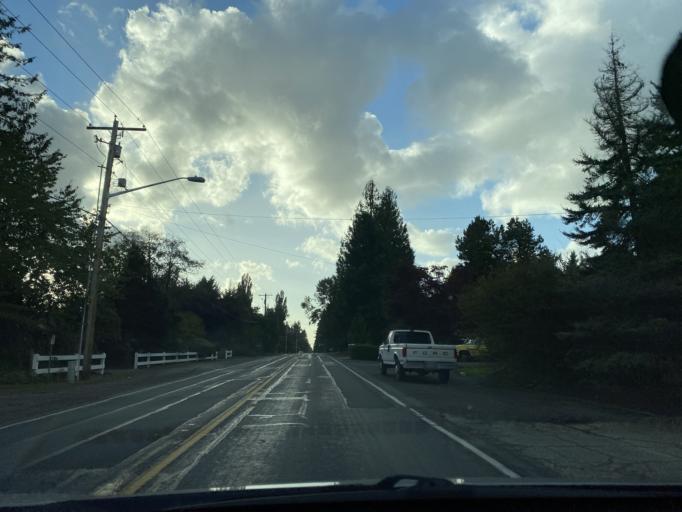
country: US
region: Washington
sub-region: Pierce County
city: South Hill
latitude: 47.1184
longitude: -122.2790
